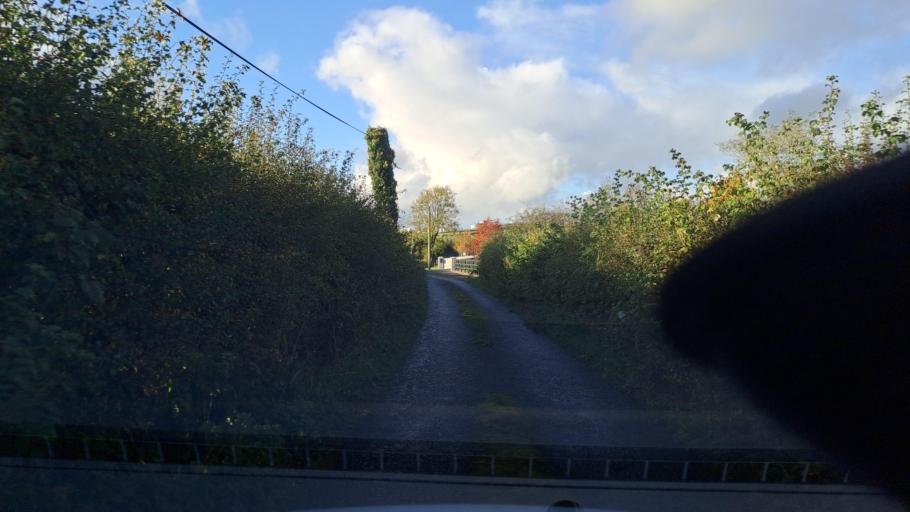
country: IE
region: Ulster
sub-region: An Cabhan
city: Bailieborough
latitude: 53.9288
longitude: -6.9399
